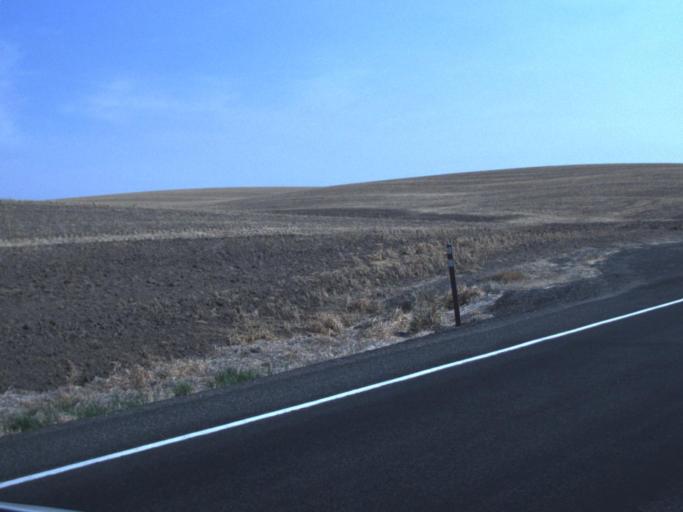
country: US
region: Idaho
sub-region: Benewah County
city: Plummer
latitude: 47.2314
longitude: -117.0570
